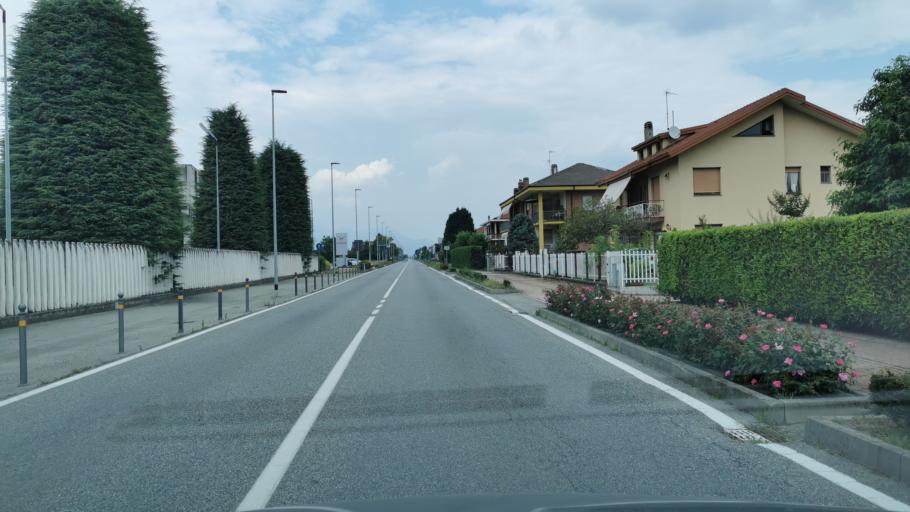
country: IT
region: Piedmont
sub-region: Provincia di Torino
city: Cavour
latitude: 44.7934
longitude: 7.3748
